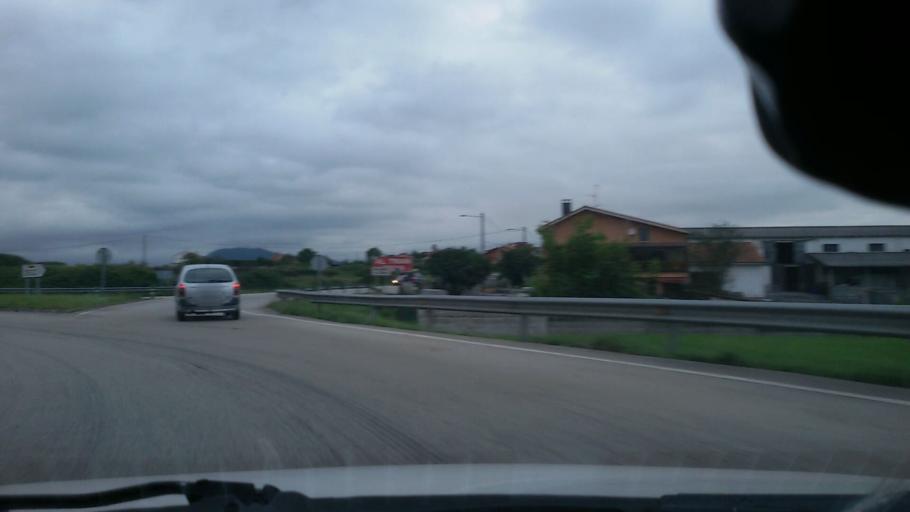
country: ES
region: Asturias
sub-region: Province of Asturias
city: Norena
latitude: 43.3914
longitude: -5.7529
